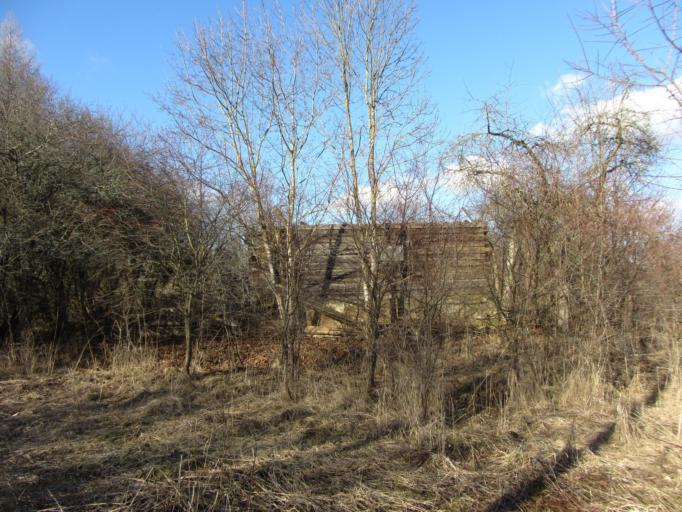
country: LT
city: Moletai
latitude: 55.1467
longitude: 25.1917
